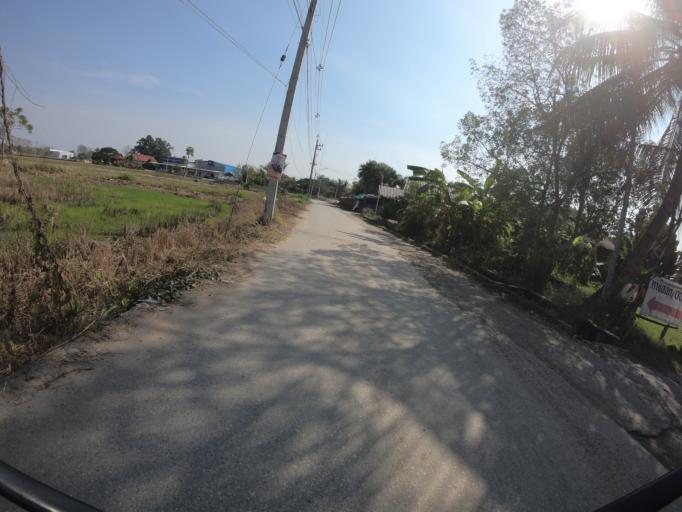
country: TH
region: Chiang Mai
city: San Sai
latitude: 18.8566
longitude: 98.9977
